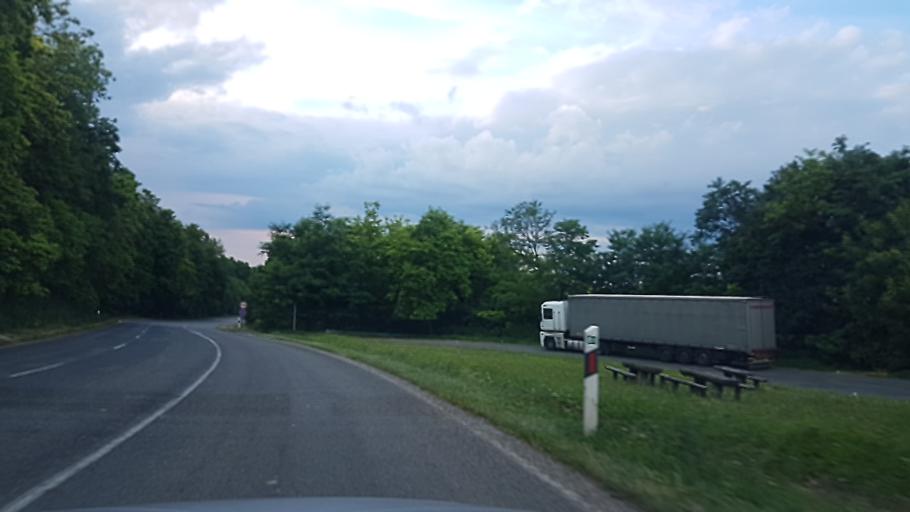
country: HU
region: Somogy
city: Kaposvar
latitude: 46.2704
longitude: 17.8249
